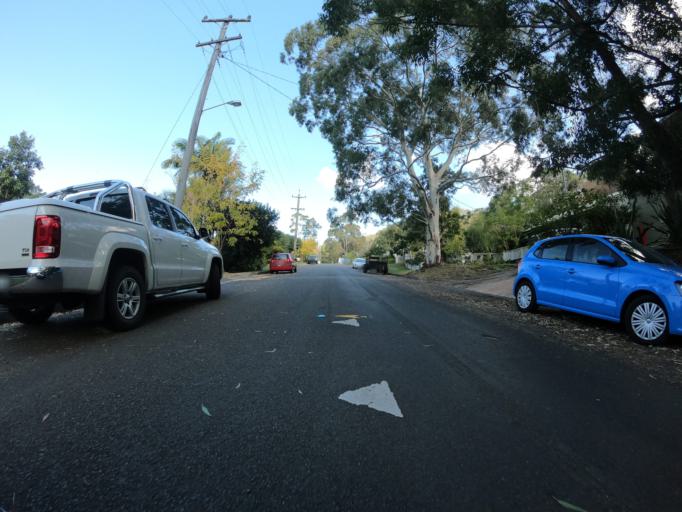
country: AU
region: New South Wales
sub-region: Wollongong
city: Cordeaux Heights
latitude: -34.4302
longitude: 150.8177
